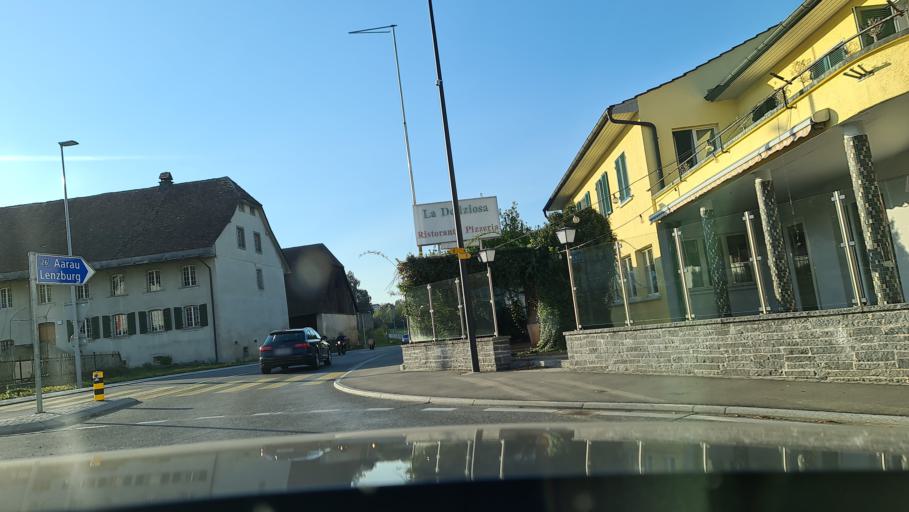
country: CH
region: Aargau
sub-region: Bezirk Lenzburg
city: Boniswil
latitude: 47.3161
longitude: 8.1854
